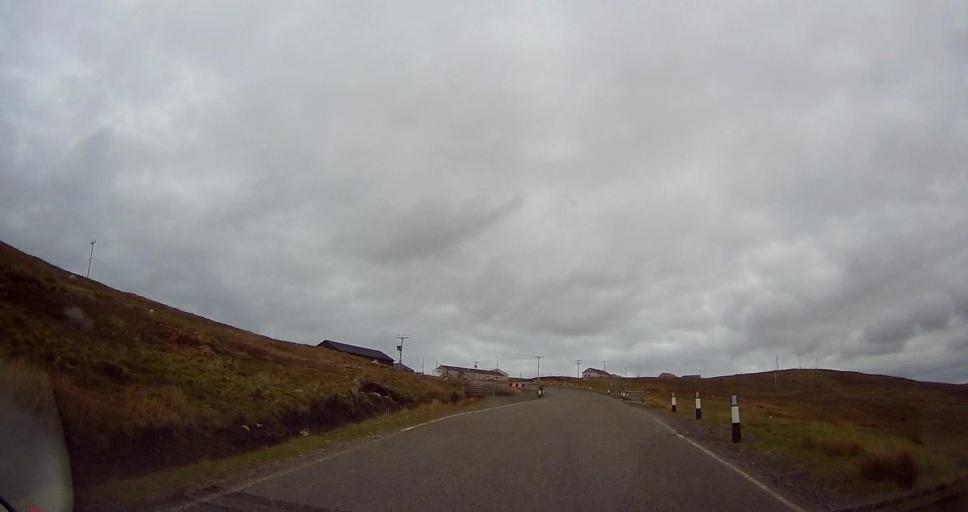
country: GB
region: Scotland
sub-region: Shetland Islands
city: Shetland
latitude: 60.6005
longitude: -1.0795
